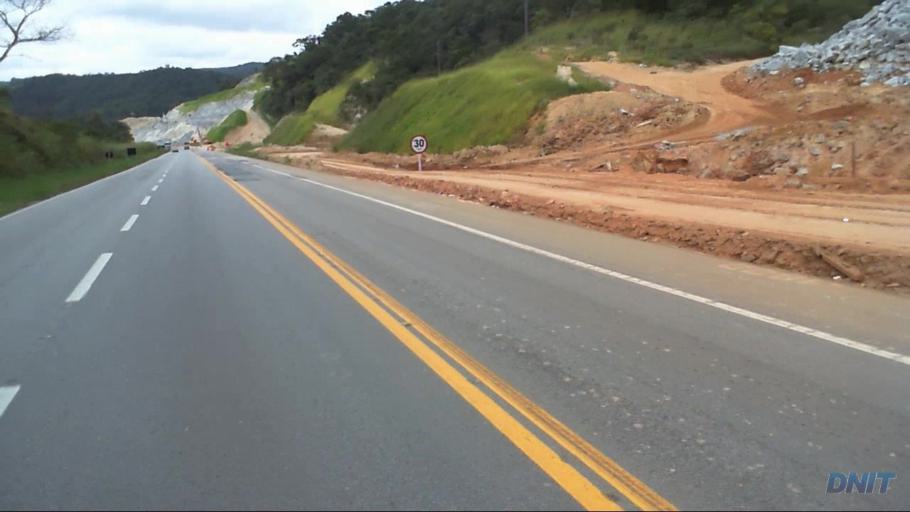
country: BR
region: Minas Gerais
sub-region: Caete
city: Caete
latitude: -19.7877
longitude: -43.6713
